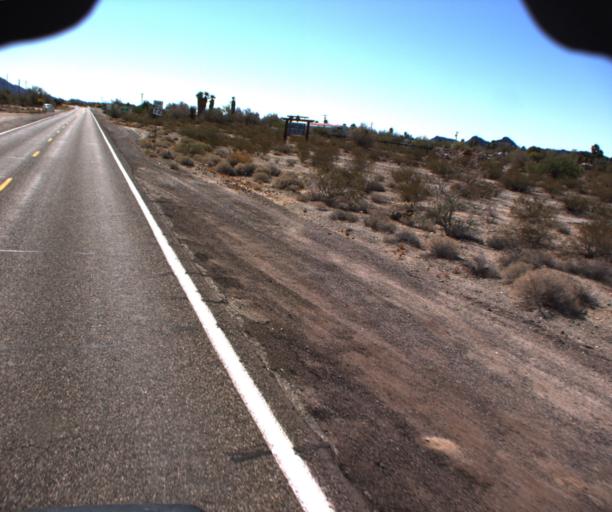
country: US
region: Arizona
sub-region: La Paz County
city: Salome
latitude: 33.7256
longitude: -113.7074
